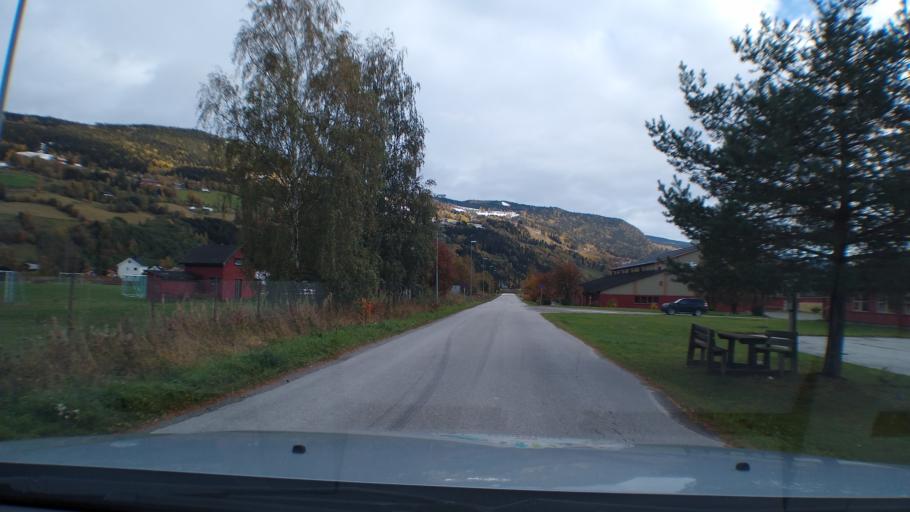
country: NO
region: Oppland
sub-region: Ringebu
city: Ringebu
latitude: 61.5258
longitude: 10.1430
